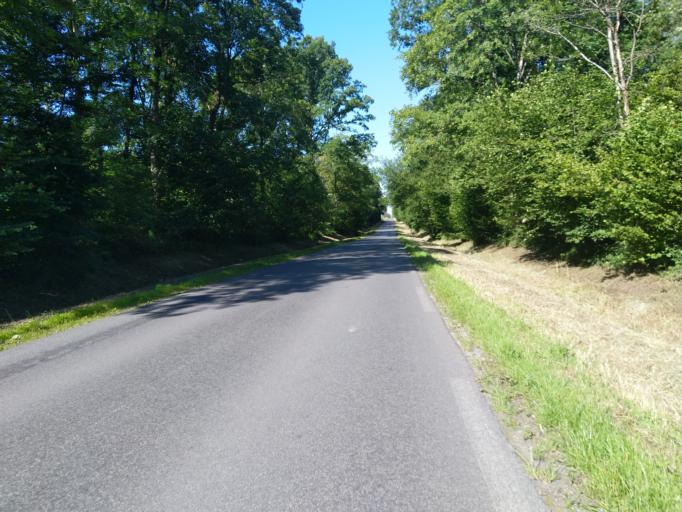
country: FR
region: Nord-Pas-de-Calais
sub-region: Departement du Nord
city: Feignies
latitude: 50.3239
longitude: 3.8920
